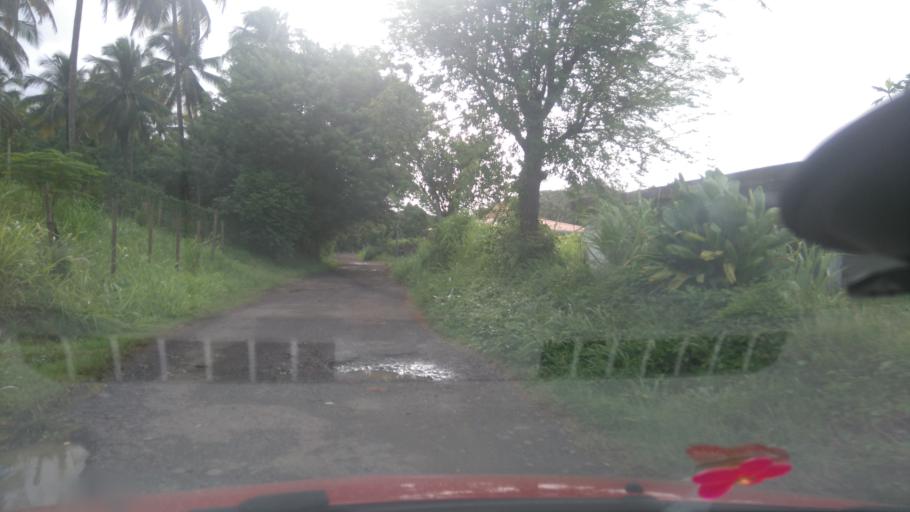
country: MQ
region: Martinique
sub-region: Martinique
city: Ducos
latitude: 14.5525
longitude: -60.9660
